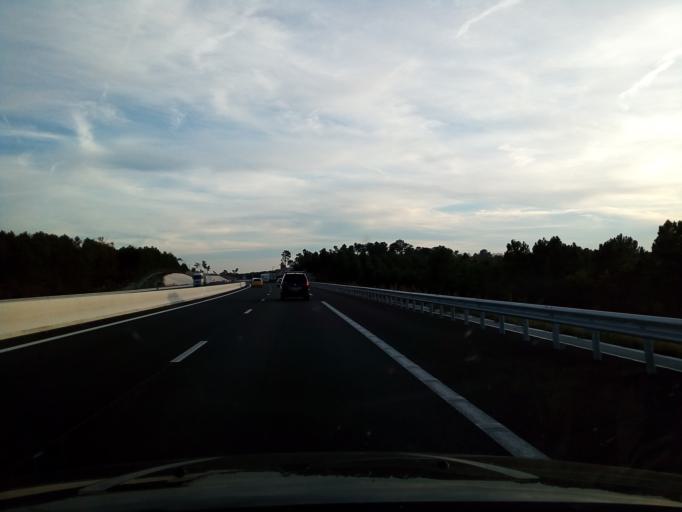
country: FR
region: Poitou-Charentes
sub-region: Departement de la Charente
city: Baignes-Sainte-Radegonde
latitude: 45.3791
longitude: -0.1820
